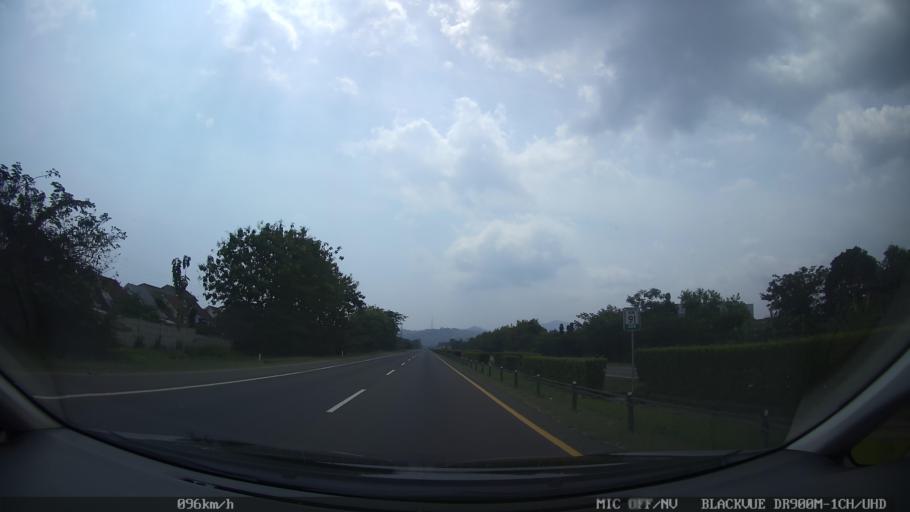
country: ID
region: Banten
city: Pangarengan
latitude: -6.0009
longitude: 106.0613
